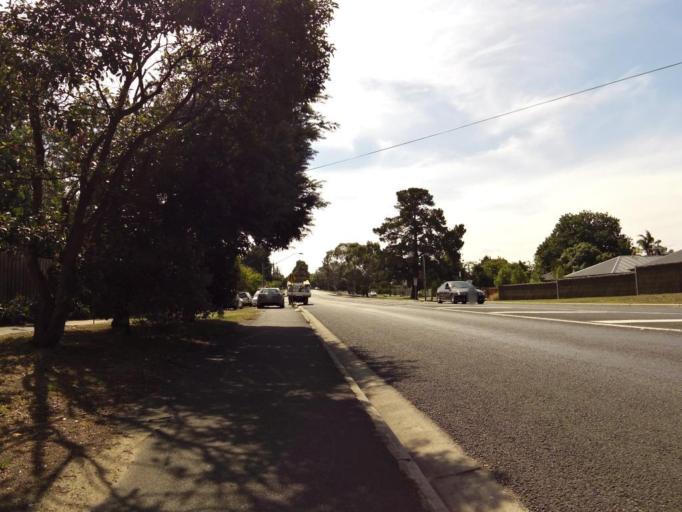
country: AU
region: Victoria
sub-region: Mornington Peninsula
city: Tyabb
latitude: -38.2311
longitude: 145.1823
